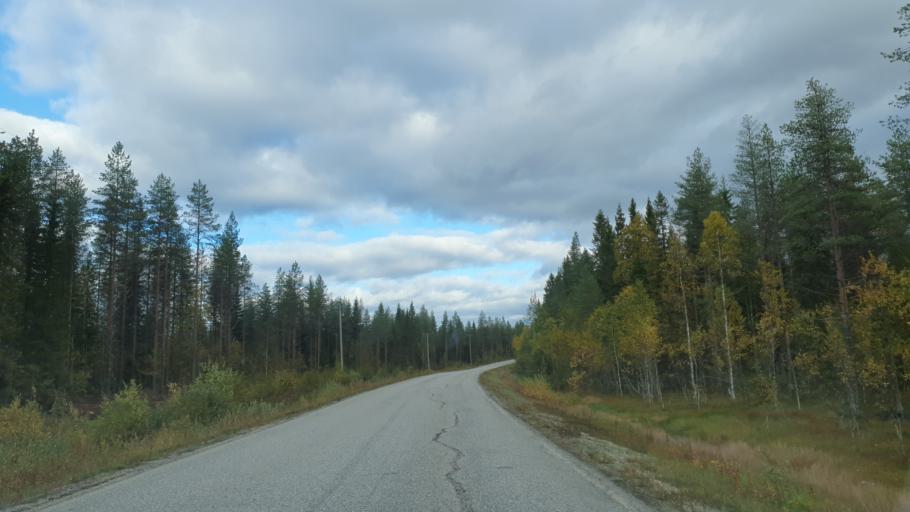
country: FI
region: Kainuu
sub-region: Kehys-Kainuu
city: Kuhmo
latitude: 63.9514
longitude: 29.8305
